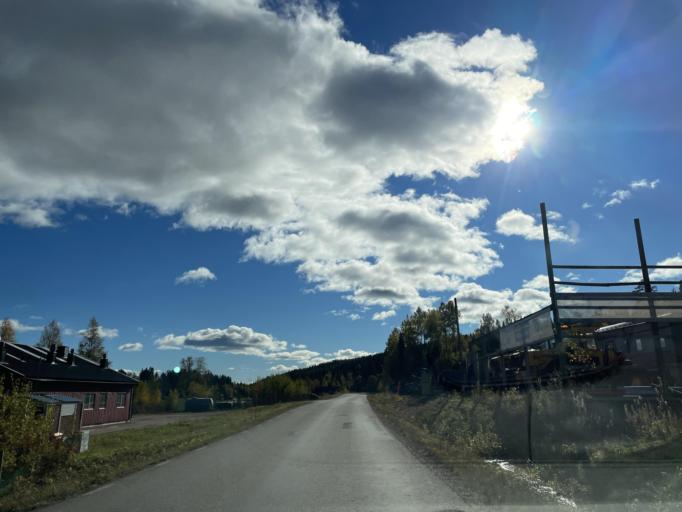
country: SE
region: Dalarna
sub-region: Malung-Saelens kommun
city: Malung
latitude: 61.1442
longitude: 13.2698
